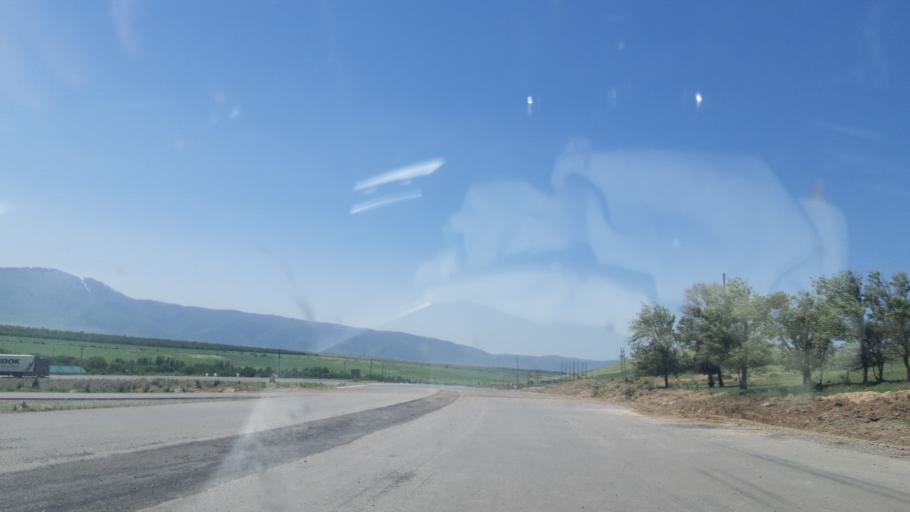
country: KZ
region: Ongtustik Qazaqstan
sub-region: Tulkibas Audany
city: Zhabagly
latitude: 42.5165
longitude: 70.5334
